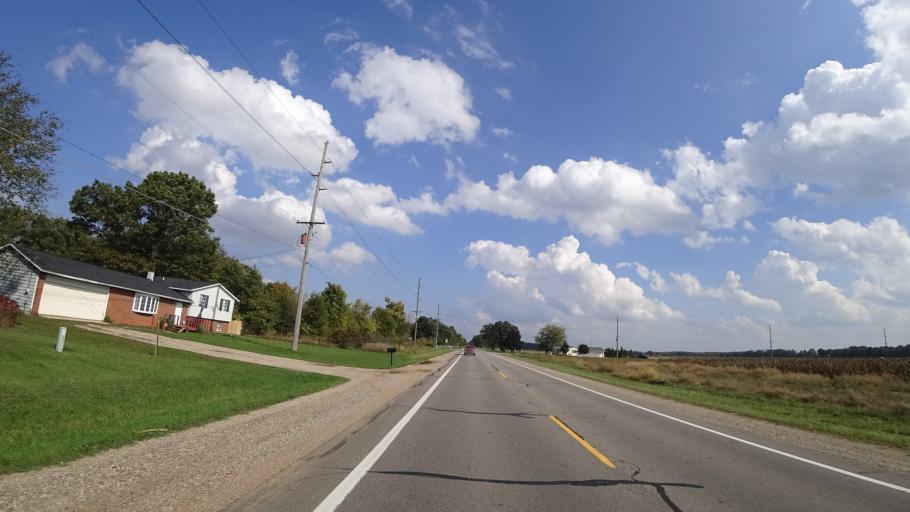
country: US
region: Michigan
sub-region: Saint Joseph County
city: Three Rivers
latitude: 41.9548
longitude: -85.6070
